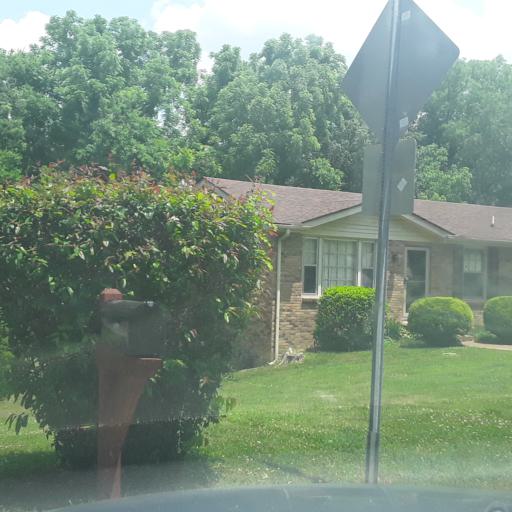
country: US
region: Tennessee
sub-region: Williamson County
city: Brentwood Estates
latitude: 36.0492
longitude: -86.6951
